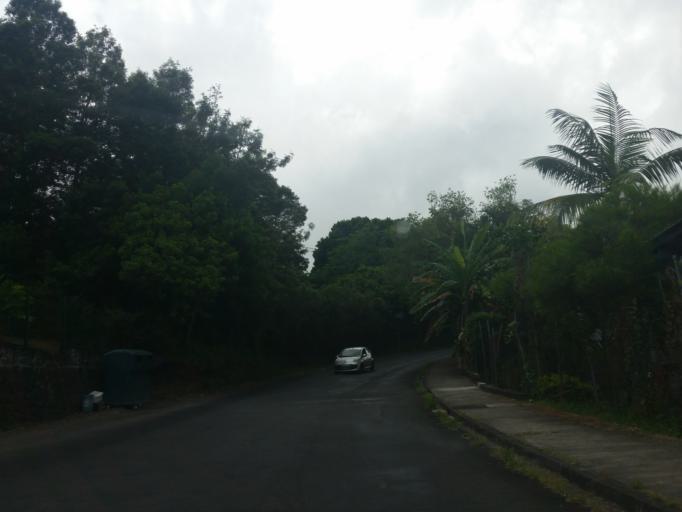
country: RE
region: Reunion
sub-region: Reunion
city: Le Tampon
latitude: -21.2546
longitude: 55.4960
